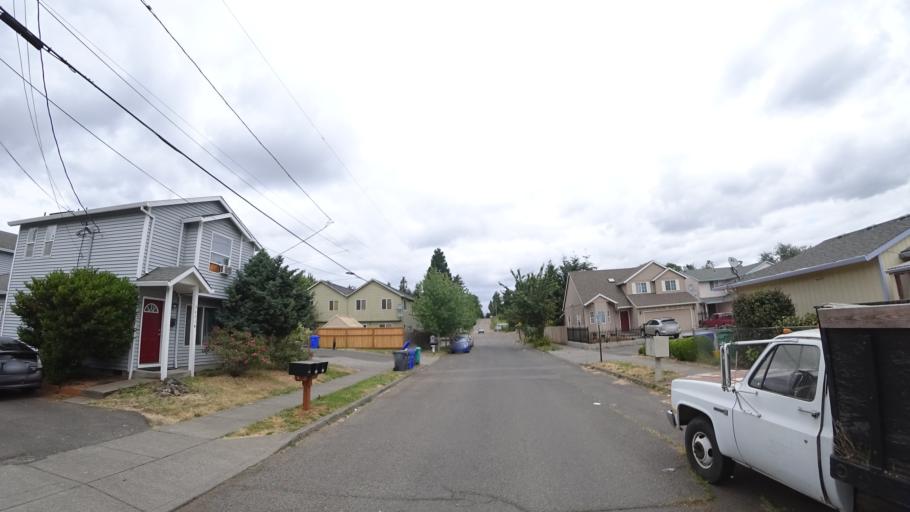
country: US
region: Oregon
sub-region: Multnomah County
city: Lents
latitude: 45.4999
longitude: -122.5718
